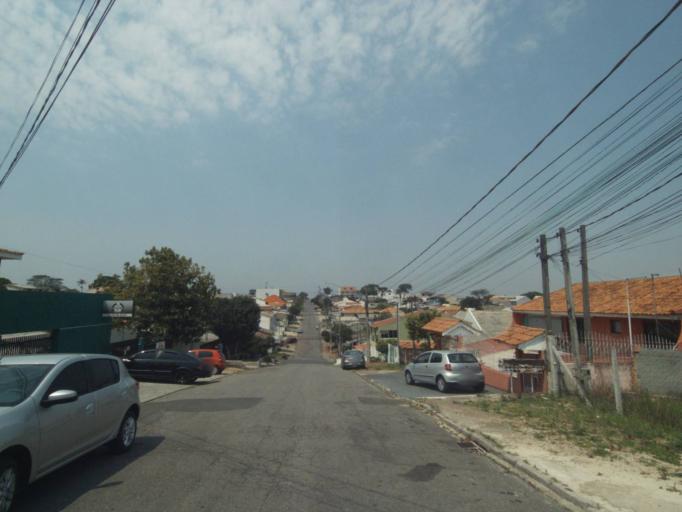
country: BR
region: Parana
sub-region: Sao Jose Dos Pinhais
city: Sao Jose dos Pinhais
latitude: -25.5338
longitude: -49.2470
